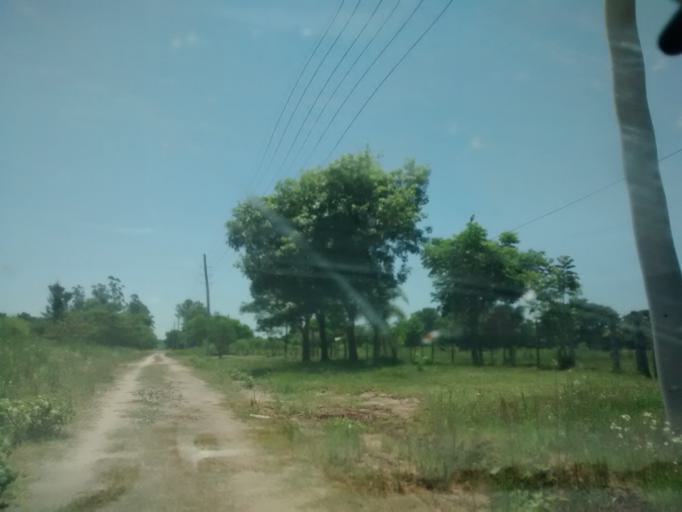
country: AR
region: Chaco
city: Fontana
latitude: -27.4213
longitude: -58.9873
